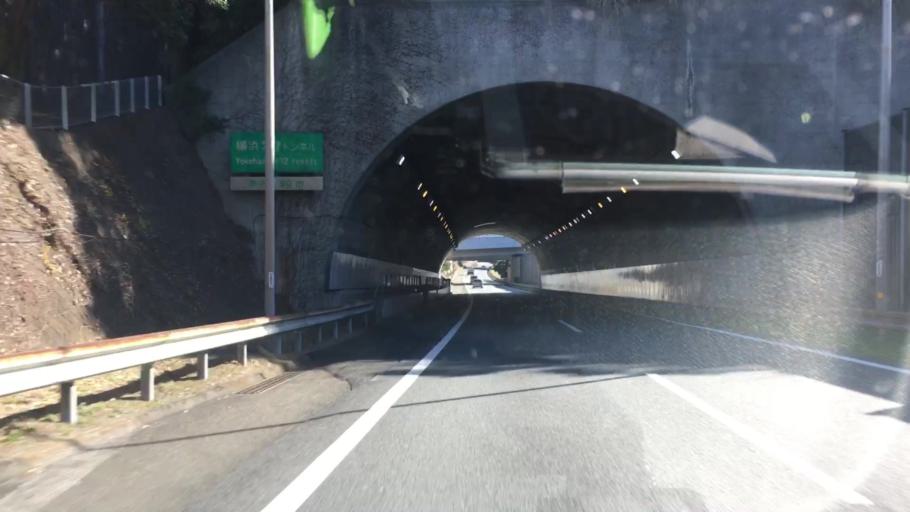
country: JP
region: Kanagawa
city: Zushi
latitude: 35.3263
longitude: 139.5974
